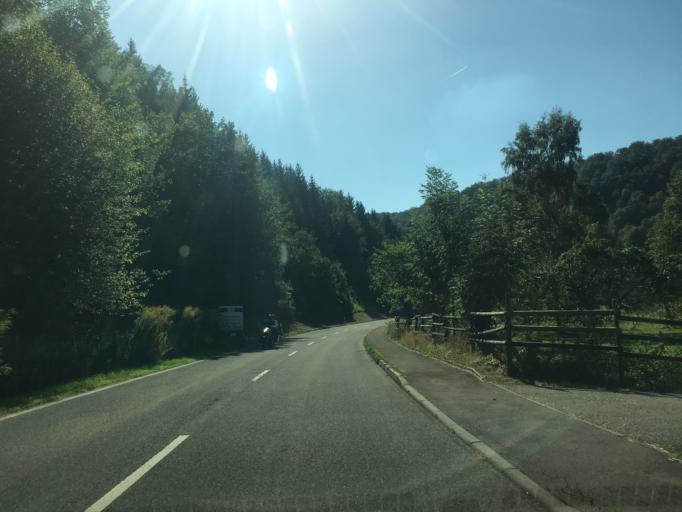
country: DE
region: Baden-Wuerttemberg
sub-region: Tuebingen Region
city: Hayingen
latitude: 48.3411
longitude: 9.4966
